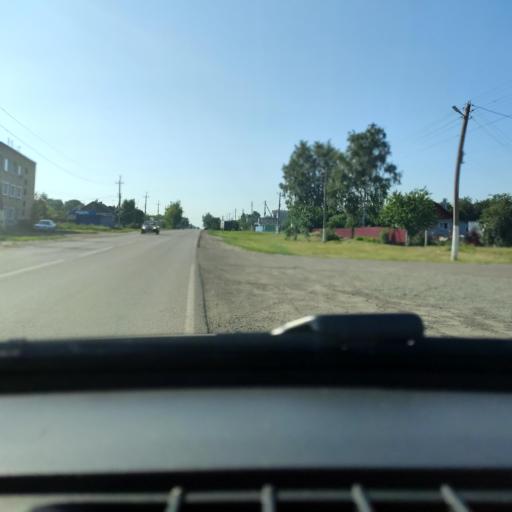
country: RU
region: Voronezj
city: Panino
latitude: 51.6472
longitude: 40.1429
